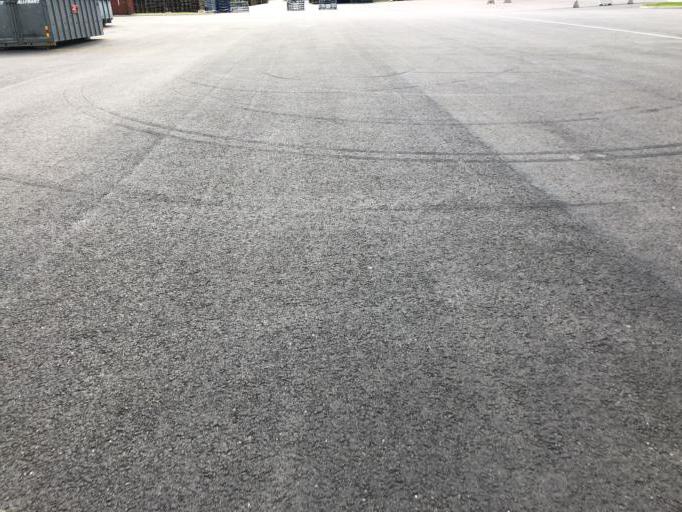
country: SE
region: Vaestra Goetaland
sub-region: Goteborg
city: Majorna
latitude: 57.7397
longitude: 11.8639
